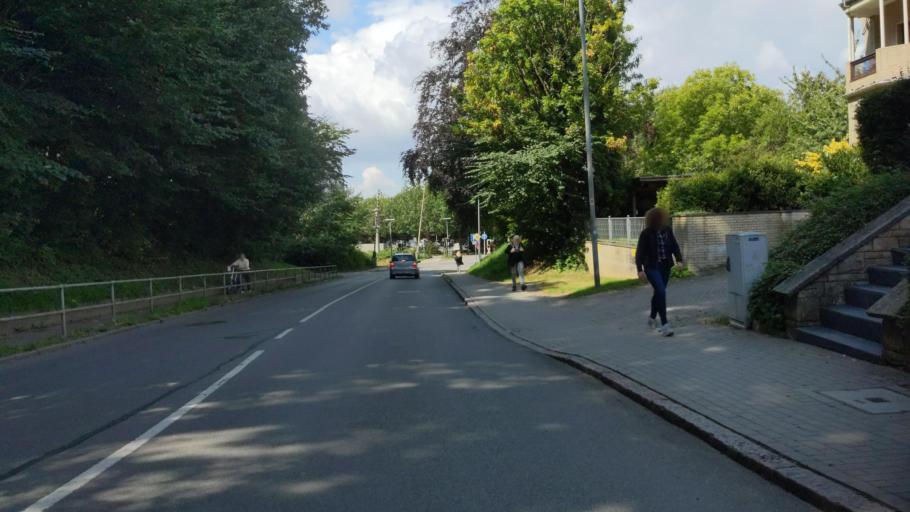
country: DE
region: Schleswig-Holstein
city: Reinfeld
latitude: 53.8286
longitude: 10.4927
